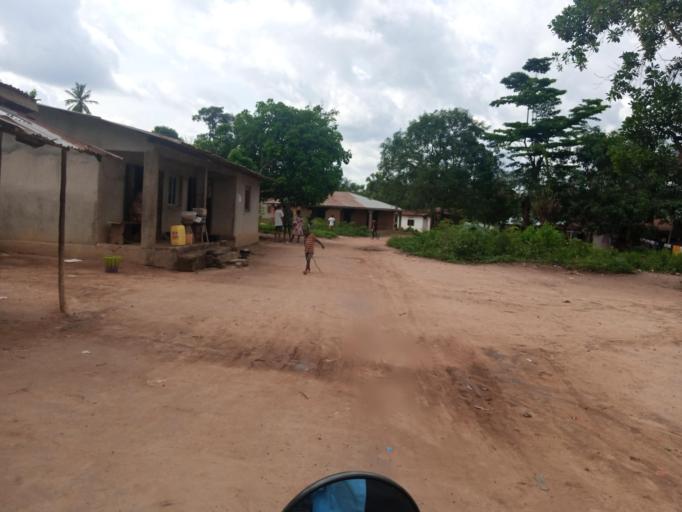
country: SL
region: Southern Province
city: Baoma
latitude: 7.9861
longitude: -11.7290
